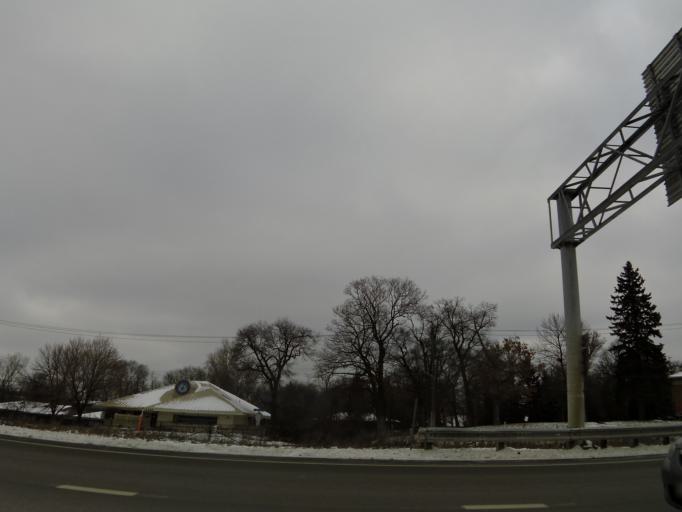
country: US
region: Minnesota
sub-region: Hennepin County
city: Minnetonka Mills
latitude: 44.9730
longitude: -93.4122
